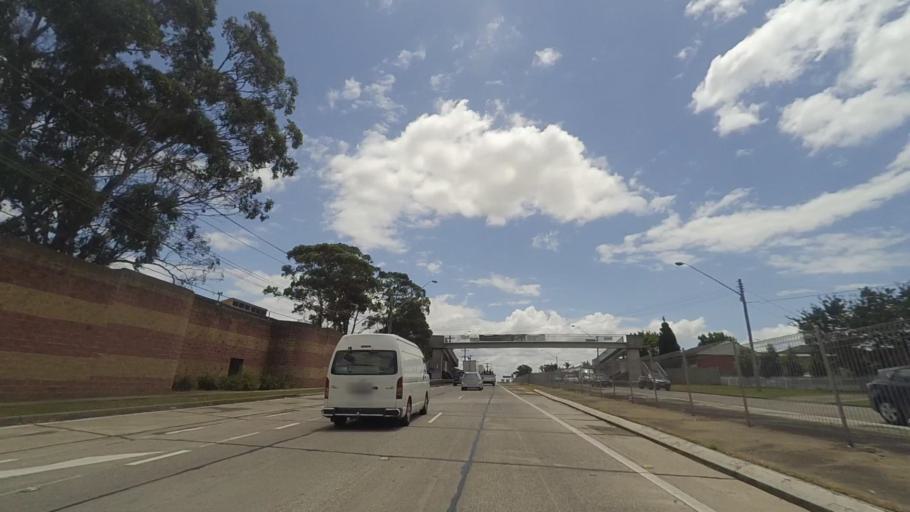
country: AU
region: New South Wales
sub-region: Fairfield
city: Fairfield Heights
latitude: -33.8683
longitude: 150.9254
